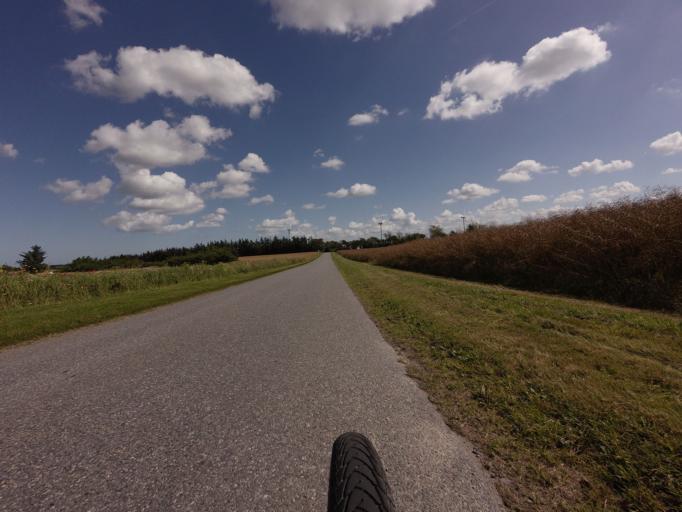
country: DK
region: North Denmark
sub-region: Hjorring Kommune
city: Hjorring
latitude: 57.4909
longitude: 9.8988
